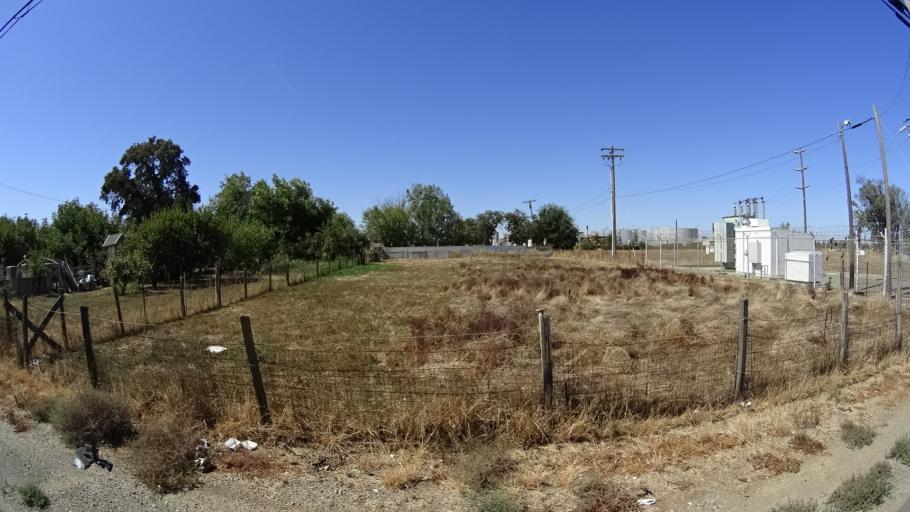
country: US
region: California
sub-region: Sacramento County
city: Elk Grove
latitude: 38.3901
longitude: -121.3529
